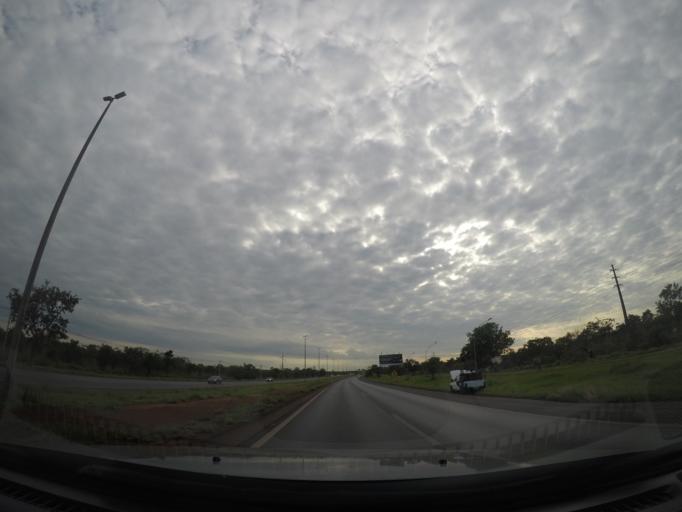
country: BR
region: Goias
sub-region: Planaltina
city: Planaltina
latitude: -15.5946
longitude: -47.6620
